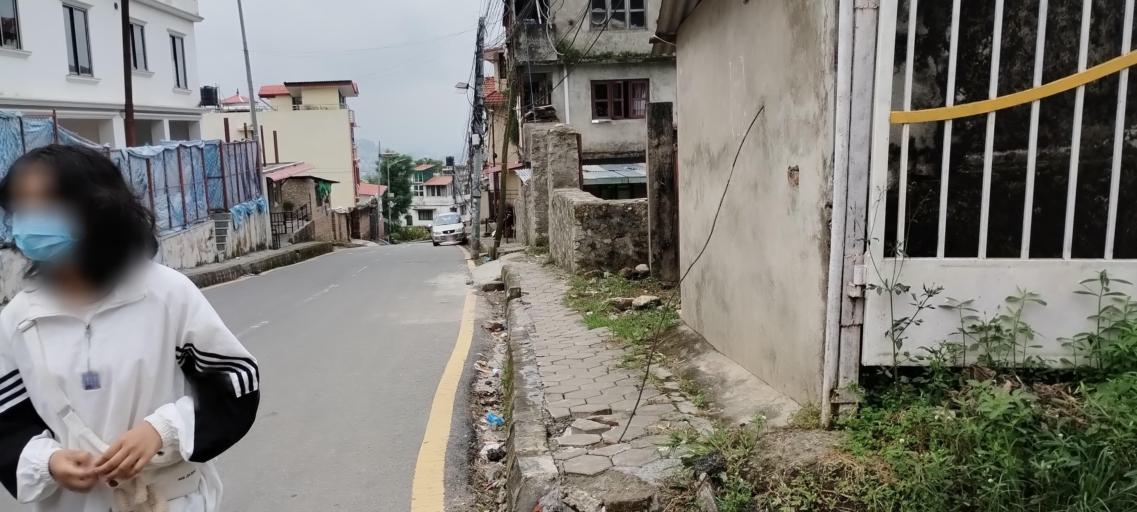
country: NP
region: Central Region
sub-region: Bagmati Zone
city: Kathmandu
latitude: 27.7814
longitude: 85.3638
